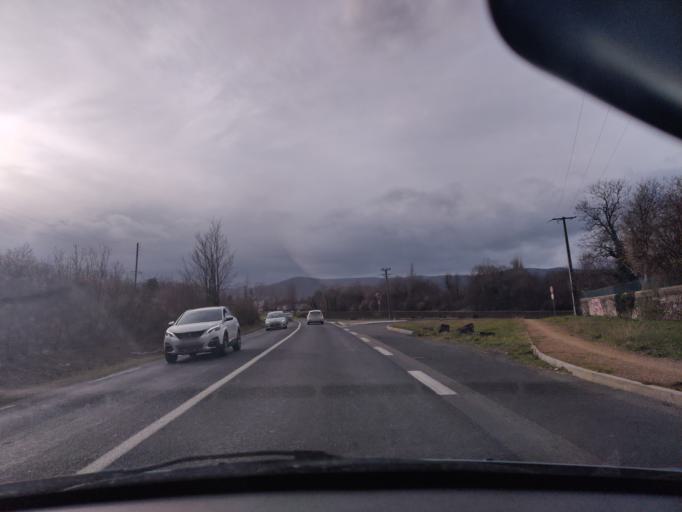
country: FR
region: Auvergne
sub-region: Departement du Puy-de-Dome
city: Menetrol
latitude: 45.8736
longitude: 3.1087
